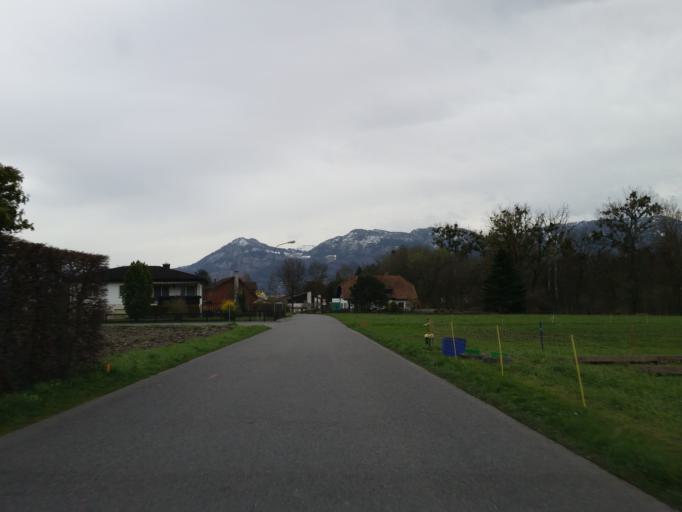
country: CH
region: Appenzell Innerrhoden
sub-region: Appenzell Inner Rhodes
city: Balgach
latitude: 47.4059
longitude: 9.6213
